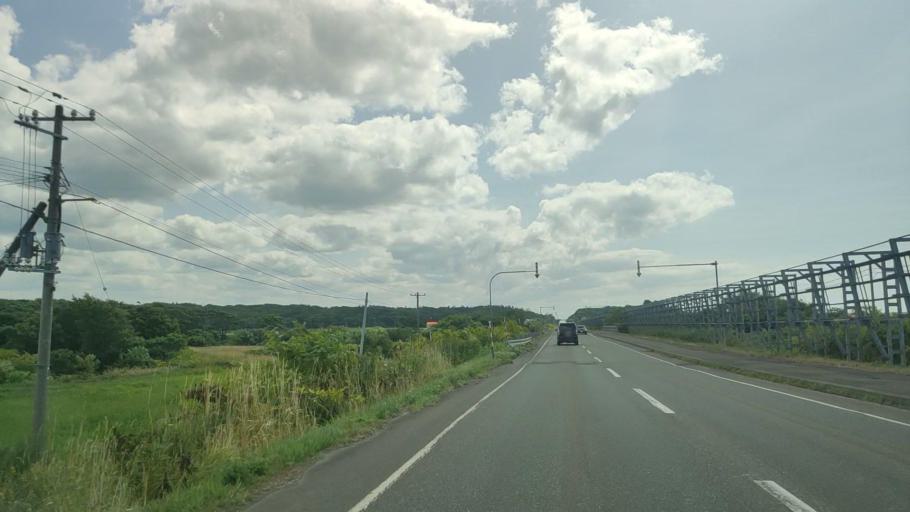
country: JP
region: Hokkaido
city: Makubetsu
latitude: 44.7747
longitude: 141.7919
